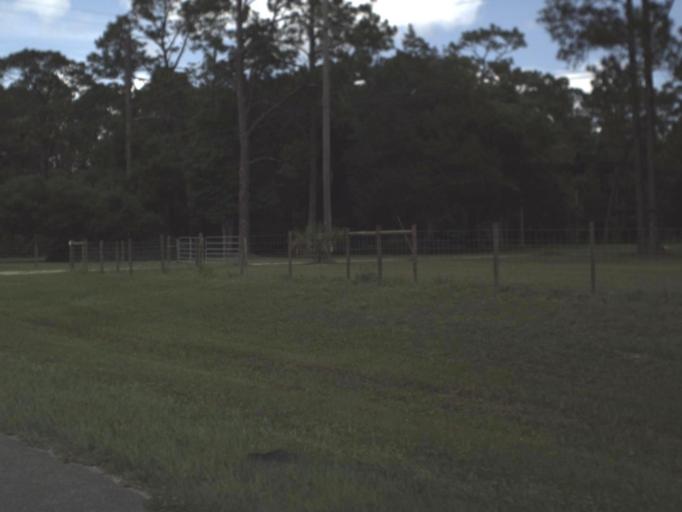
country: US
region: Florida
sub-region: Nassau County
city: Yulee
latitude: 30.6723
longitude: -81.6420
